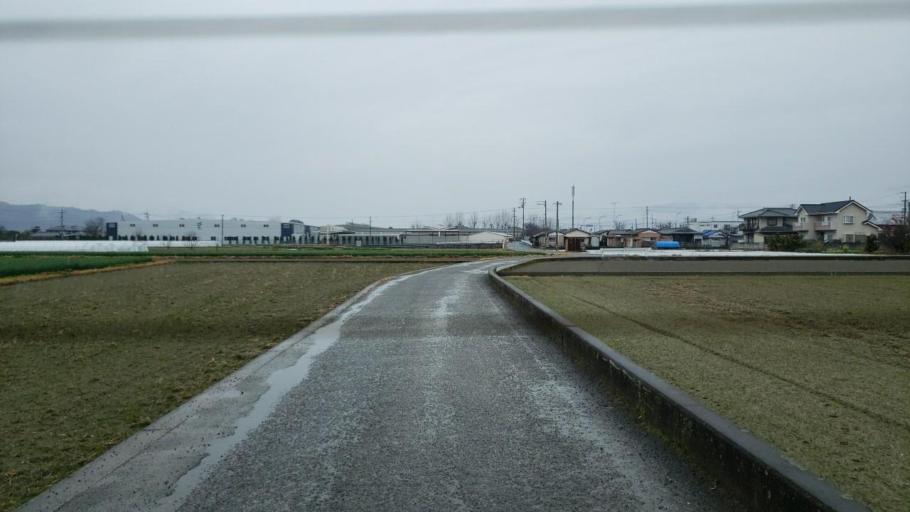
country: JP
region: Tokushima
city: Kamojimacho-jogejima
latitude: 34.0614
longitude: 134.2839
